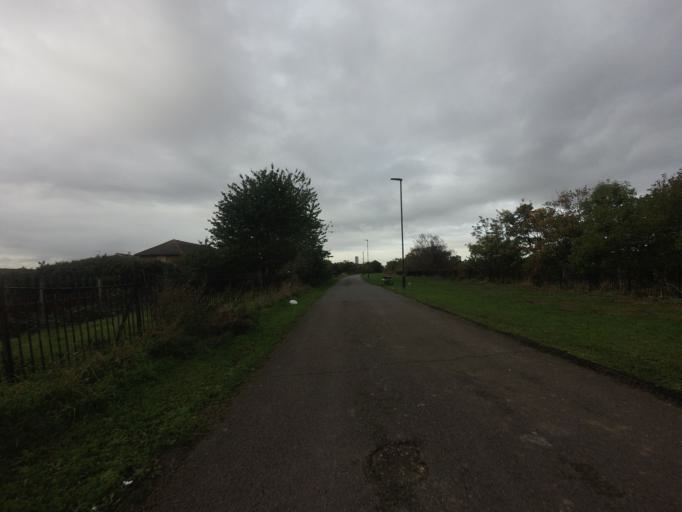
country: GB
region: England
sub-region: Greater London
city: East Ham
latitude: 51.5259
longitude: 0.0222
